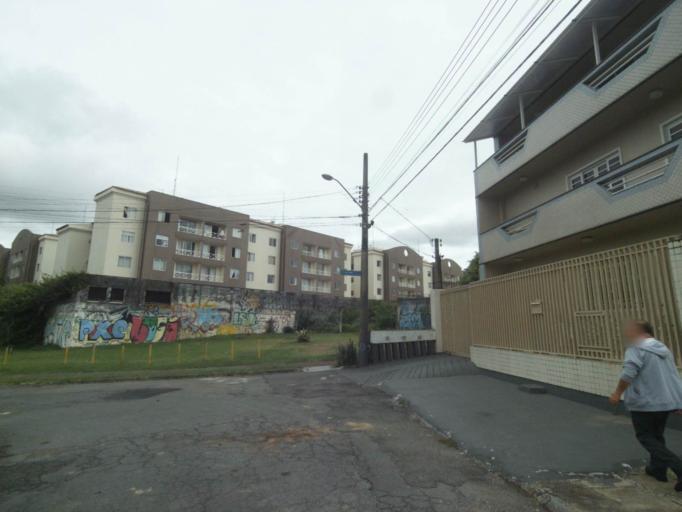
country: BR
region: Parana
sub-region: Curitiba
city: Curitiba
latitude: -25.4934
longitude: -49.2846
